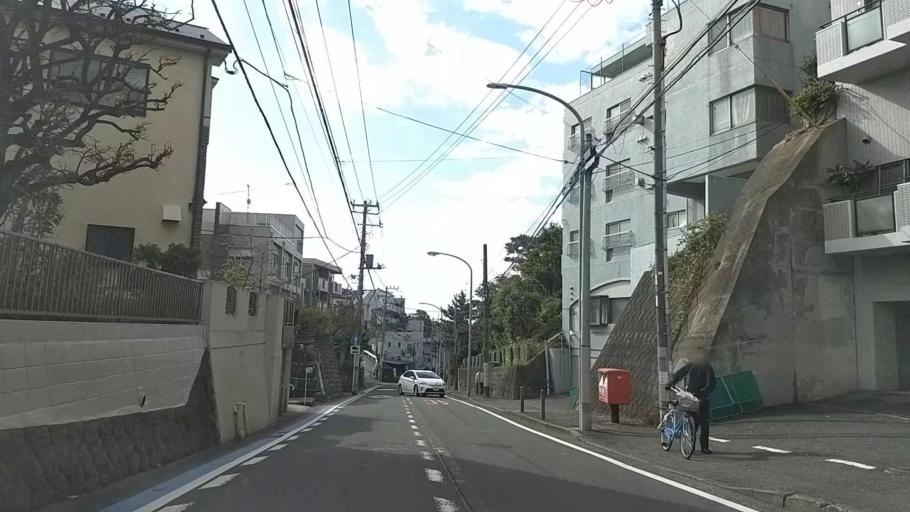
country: JP
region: Kanagawa
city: Yokohama
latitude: 35.5091
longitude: 139.6536
